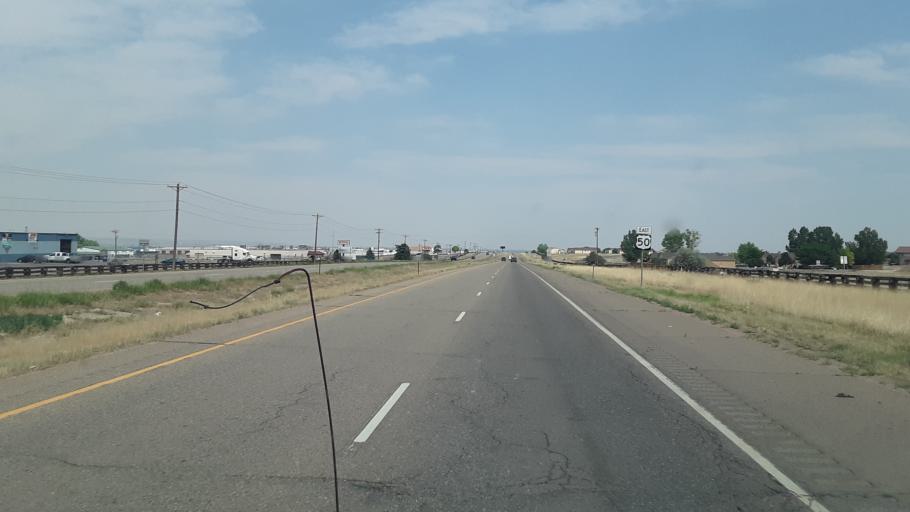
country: US
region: Colorado
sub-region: Pueblo County
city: Pueblo West
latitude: 38.3334
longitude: -104.7365
